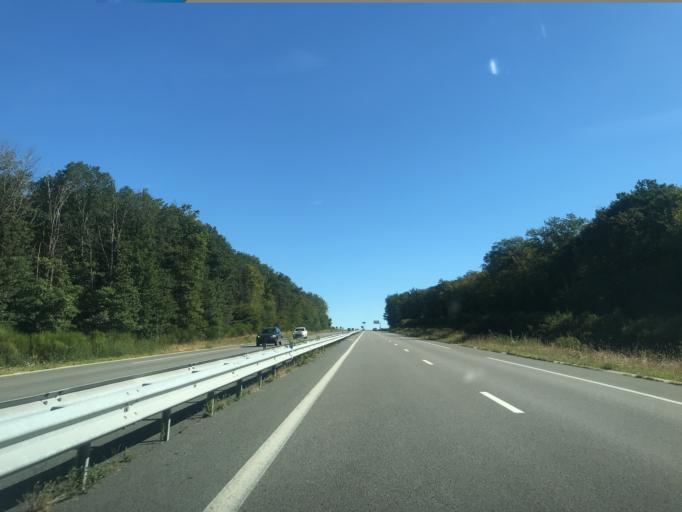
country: FR
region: Limousin
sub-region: Departement de la Creuse
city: Chambon-sur-Voueize
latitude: 46.2529
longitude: 2.3554
